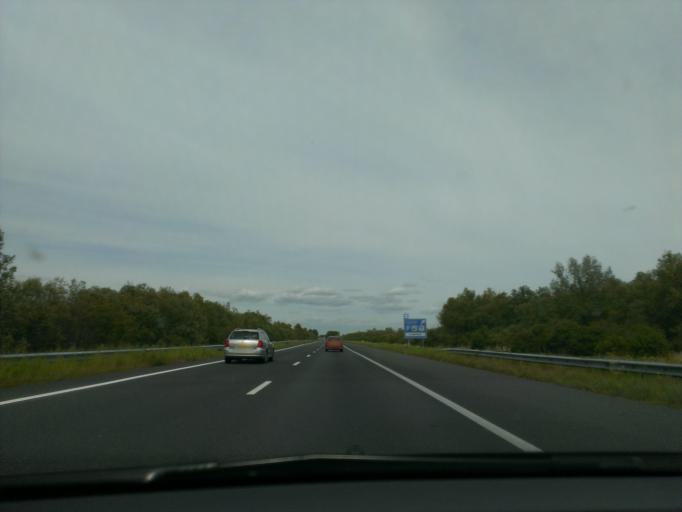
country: NL
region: Flevoland
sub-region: Gemeente Lelystad
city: Lelystad
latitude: 52.4224
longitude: 5.4022
